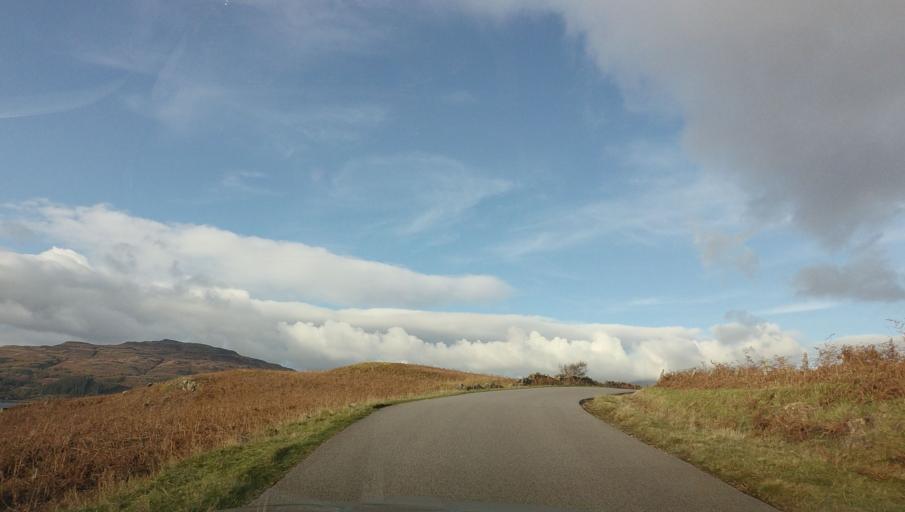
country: GB
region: Scotland
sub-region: Argyll and Bute
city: Isle Of Mull
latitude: 56.3501
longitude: -6.0866
